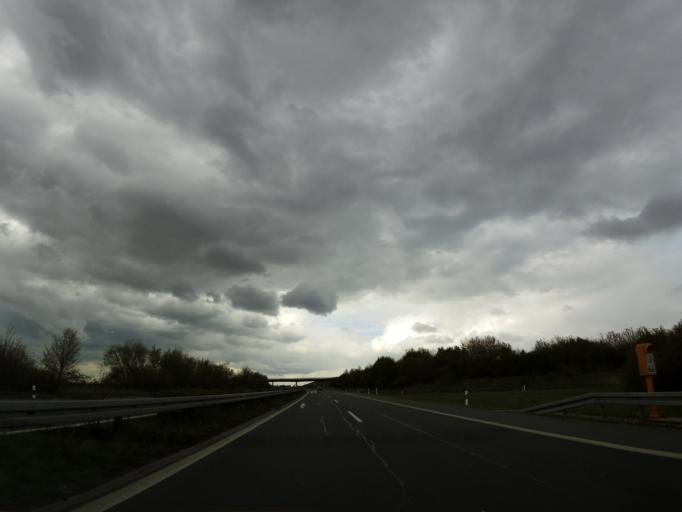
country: DE
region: Saxony-Anhalt
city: Darlingerode
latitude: 51.8721
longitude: 10.7584
